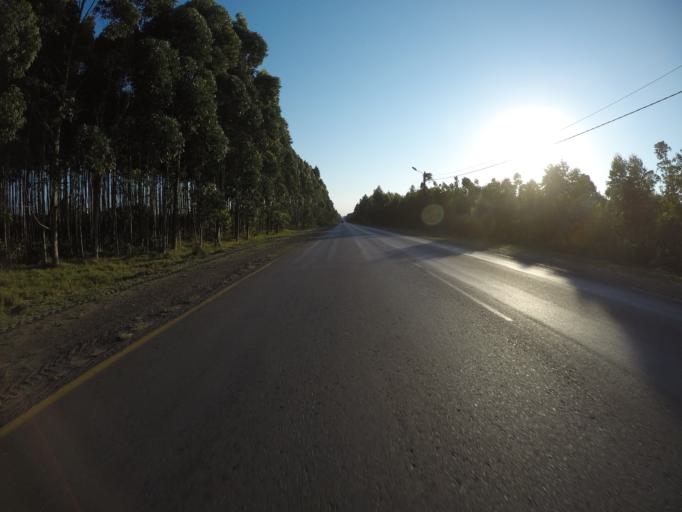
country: ZA
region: KwaZulu-Natal
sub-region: uThungulu District Municipality
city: KwaMbonambi
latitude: -28.6831
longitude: 32.1874
